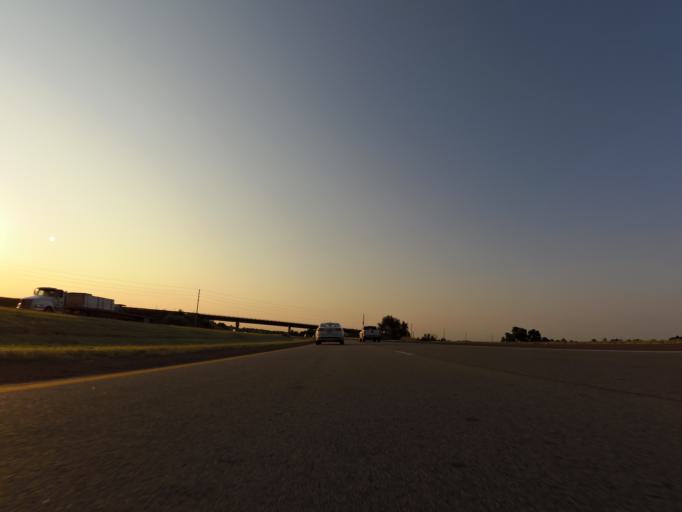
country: US
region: Kansas
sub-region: Sedgwick County
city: Maize
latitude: 37.7622
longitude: -97.4466
